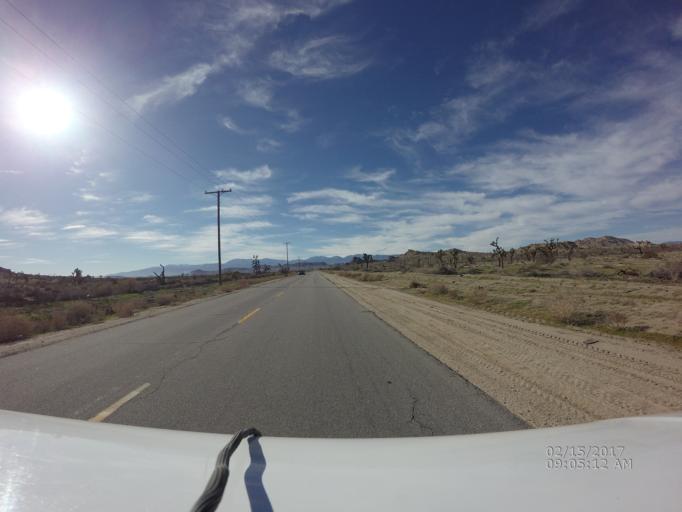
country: US
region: California
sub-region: Los Angeles County
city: Lake Los Angeles
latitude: 34.6551
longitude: -117.8630
